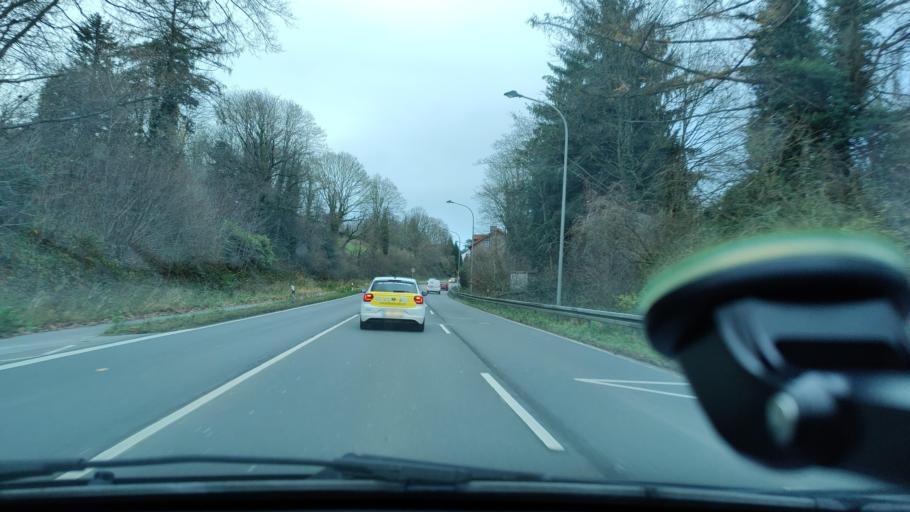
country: DE
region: North Rhine-Westphalia
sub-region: Regierungsbezirk Koln
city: Wurselen
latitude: 50.8122
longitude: 6.1173
